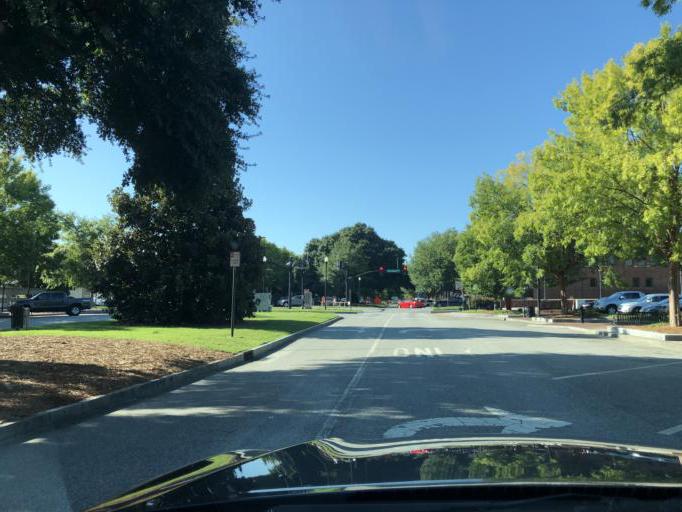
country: US
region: Alabama
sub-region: Russell County
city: Phenix City
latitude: 32.4712
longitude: -84.9933
